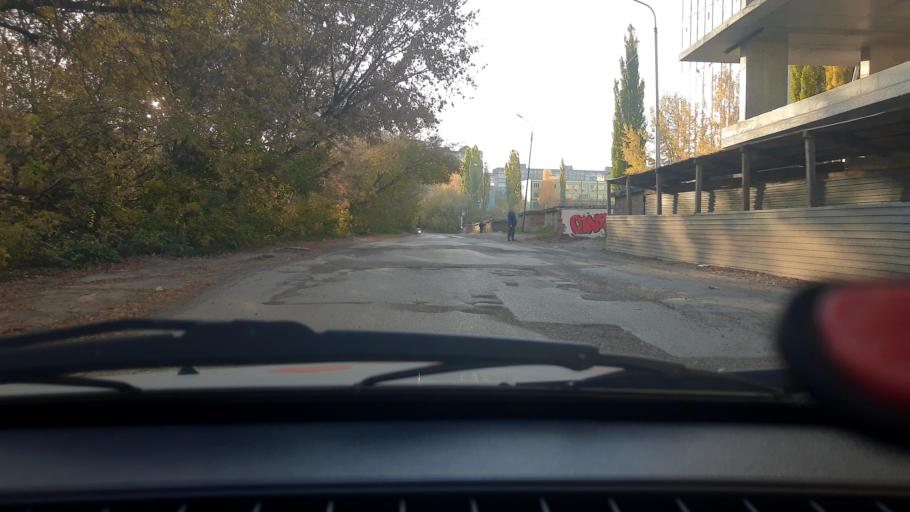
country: RU
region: Bashkortostan
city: Ufa
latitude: 54.7264
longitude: 55.9986
